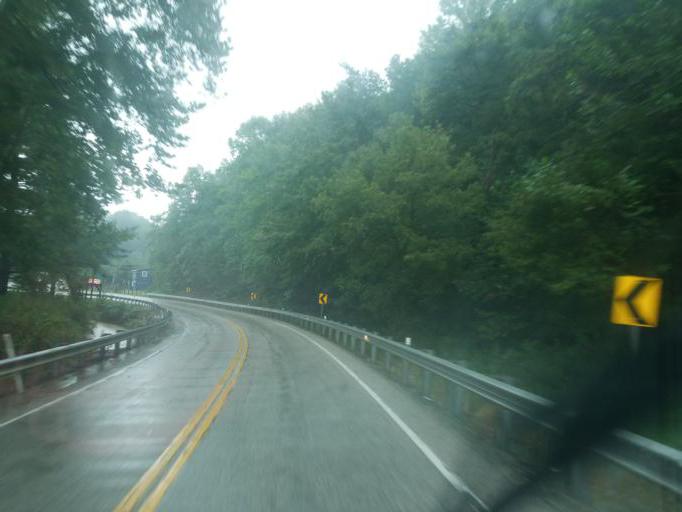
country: US
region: Kentucky
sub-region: Rowan County
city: Morehead
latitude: 38.2579
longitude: -83.3331
